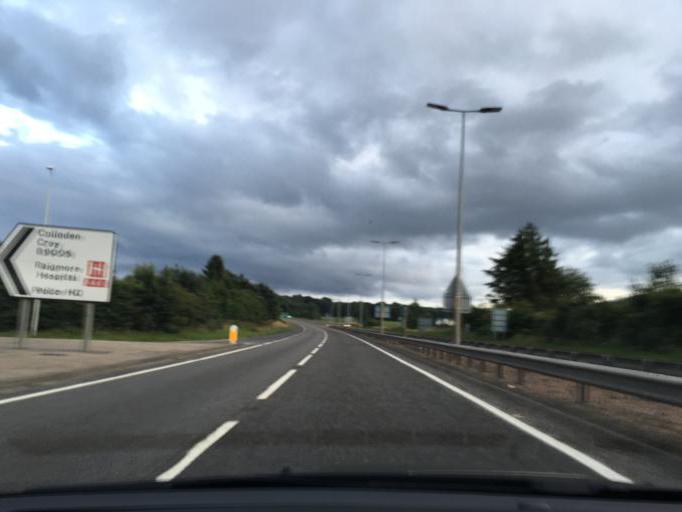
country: GB
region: Scotland
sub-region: Highland
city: Inverness
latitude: 57.4716
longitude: -4.1842
